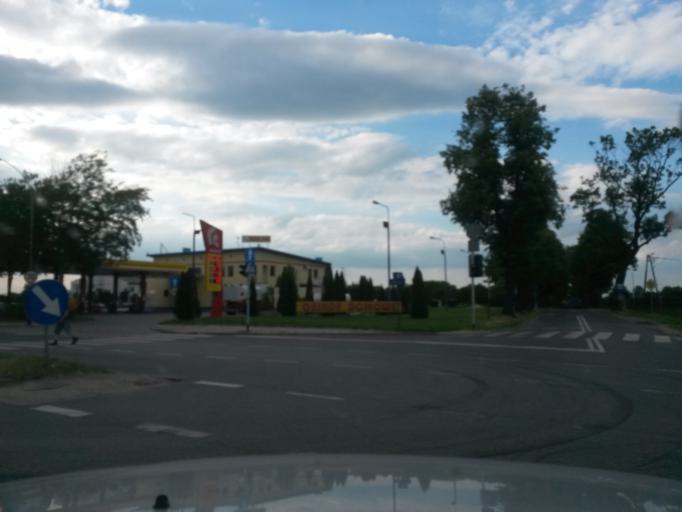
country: PL
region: Lodz Voivodeship
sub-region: Piotrkow Trybunalski
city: Piotrkow Trybunalski
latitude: 51.4076
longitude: 19.6472
